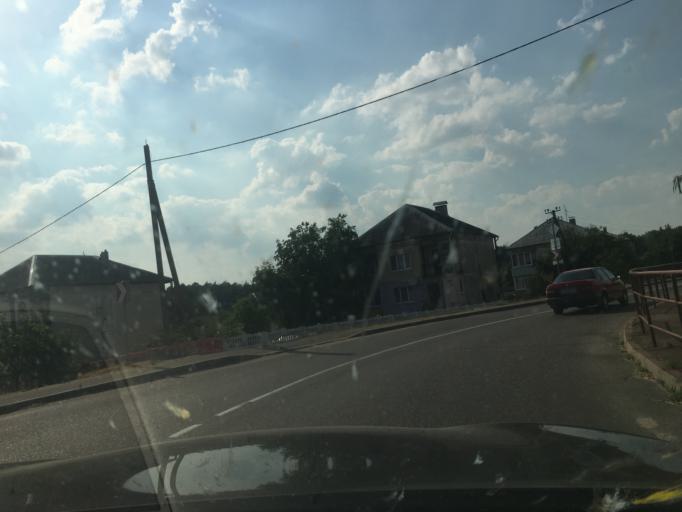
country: BY
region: Grodnenskaya
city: Vyalikaya Byerastavitsa
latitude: 53.1247
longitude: 24.0609
